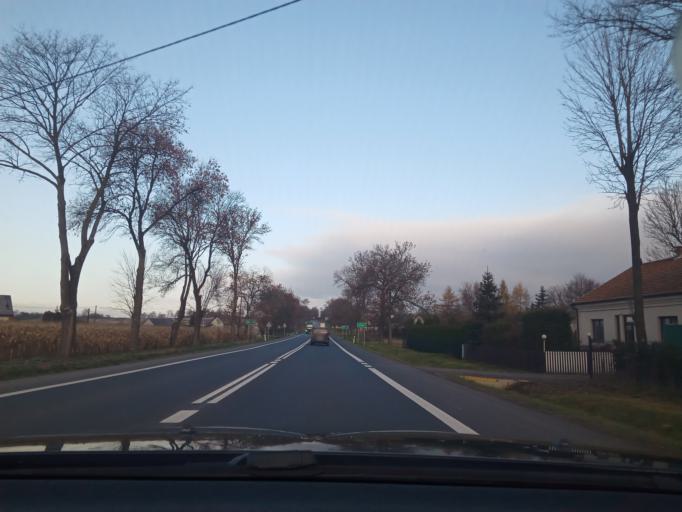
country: PL
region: Lesser Poland Voivodeship
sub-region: Powiat krakowski
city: Slomniki
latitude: 50.2863
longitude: 20.0523
